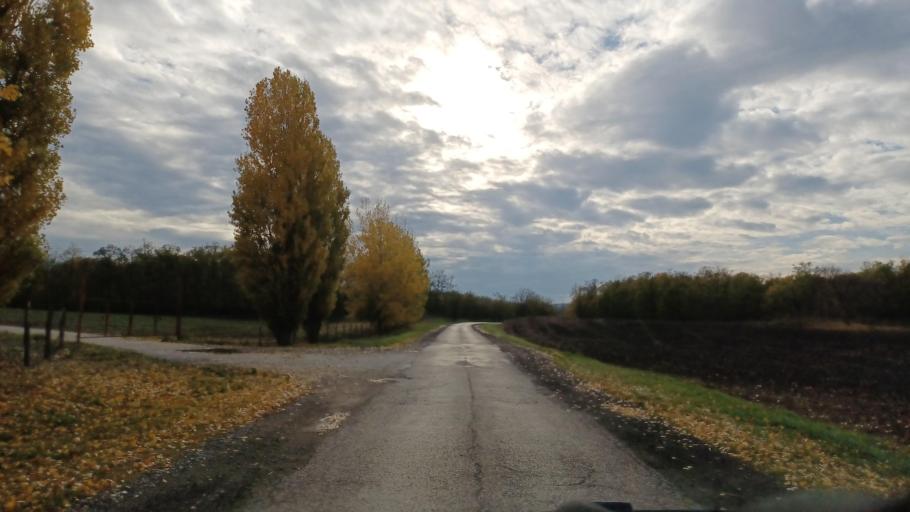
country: HU
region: Tolna
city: Simontornya
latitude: 46.7118
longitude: 18.6003
